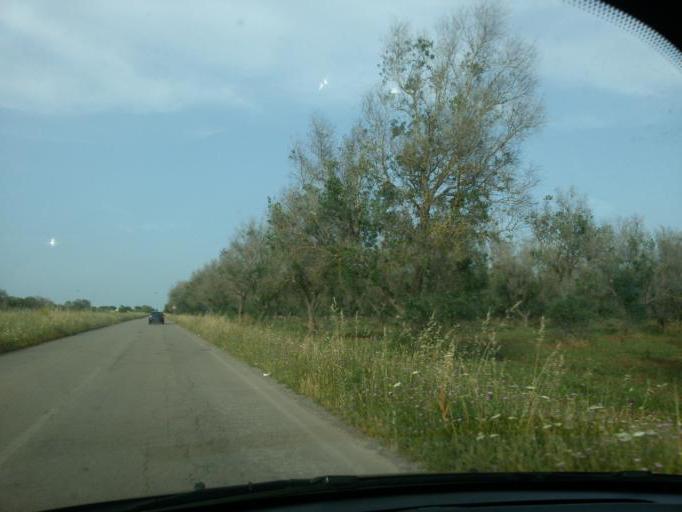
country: IT
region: Apulia
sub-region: Provincia di Brindisi
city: San Donaci
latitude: 40.4349
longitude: 17.8872
